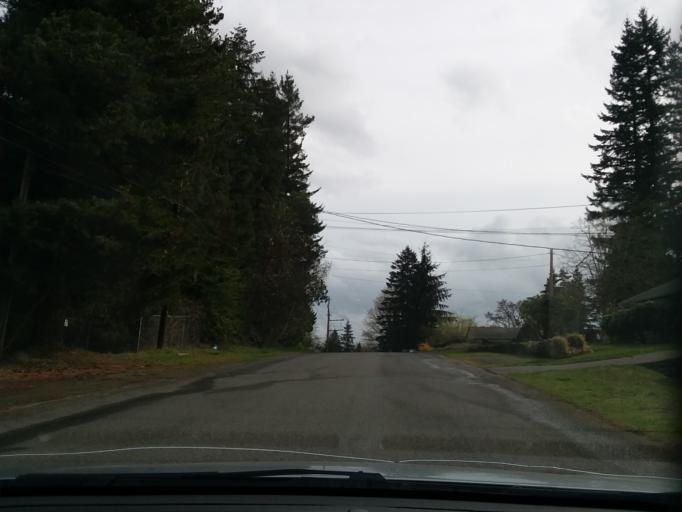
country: US
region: Washington
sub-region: Snohomish County
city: Mountlake Terrace
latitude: 47.7841
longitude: -122.3031
